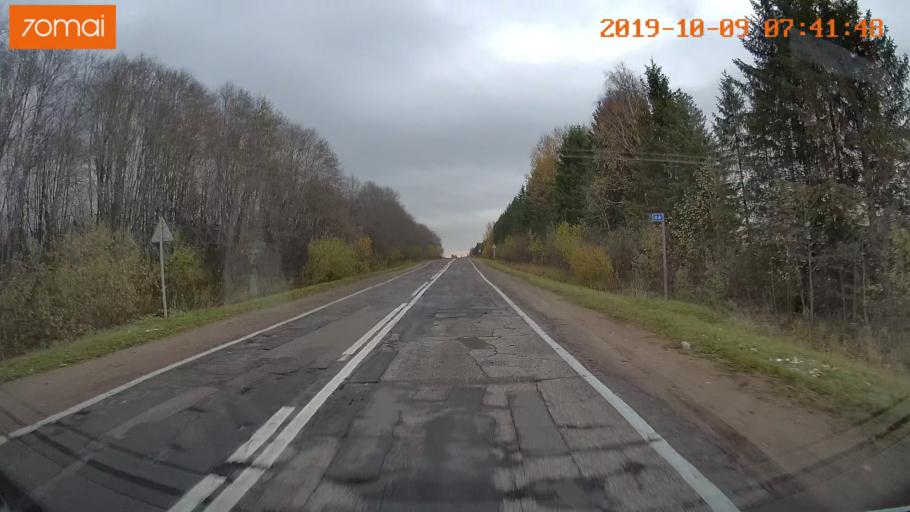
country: RU
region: Jaroslavl
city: Kukoboy
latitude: 58.6403
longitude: 39.7124
